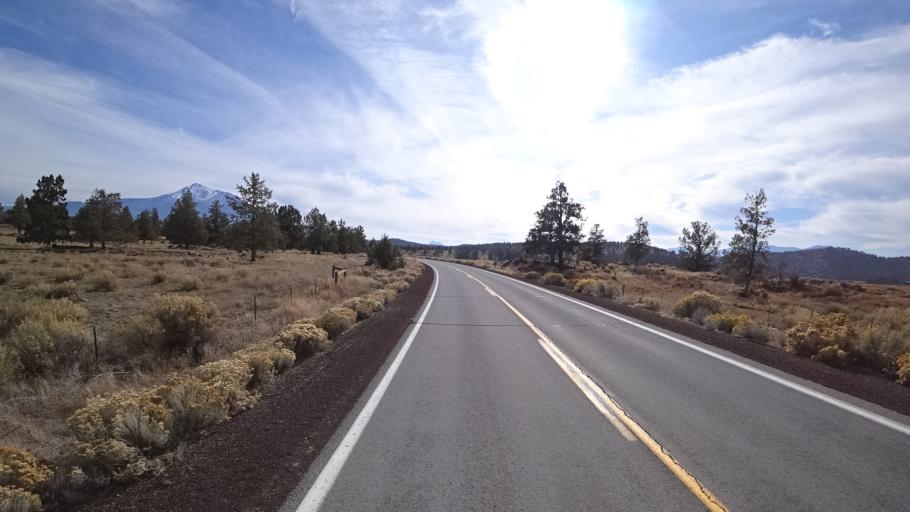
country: US
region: California
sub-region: Siskiyou County
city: Weed
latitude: 41.5586
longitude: -122.3872
